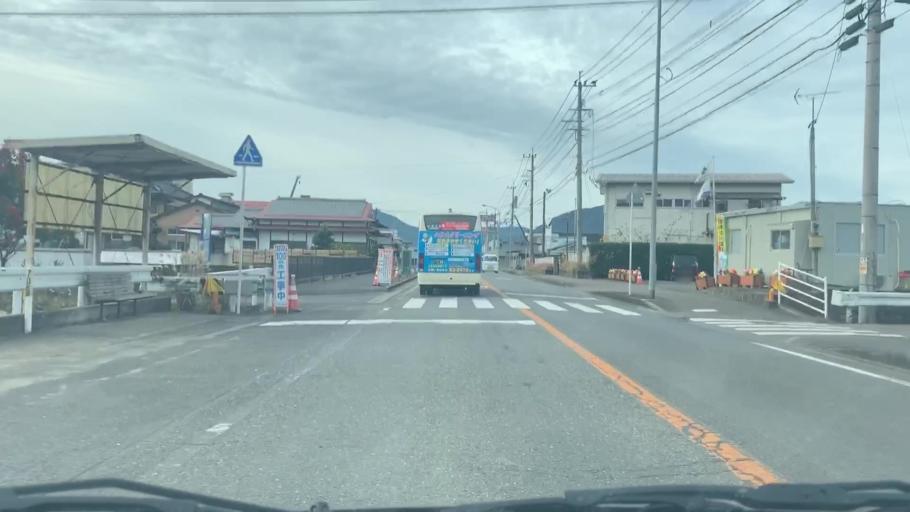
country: JP
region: Saga Prefecture
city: Ureshinomachi-shimojuku
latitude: 33.1083
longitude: 129.9984
